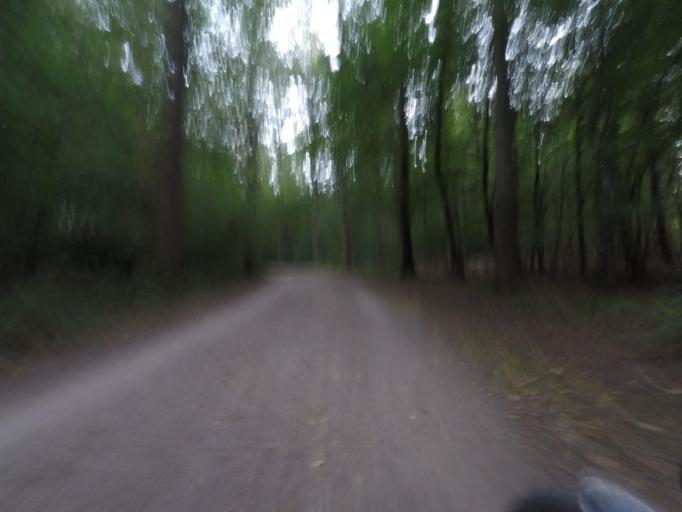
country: DE
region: Hamburg
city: Bergstedt
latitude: 53.6420
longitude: 10.1431
